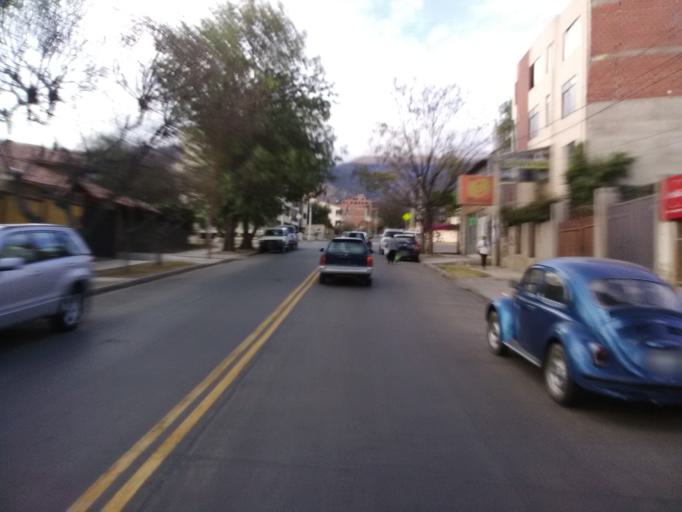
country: BO
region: Cochabamba
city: Cochabamba
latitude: -17.3673
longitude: -66.1633
